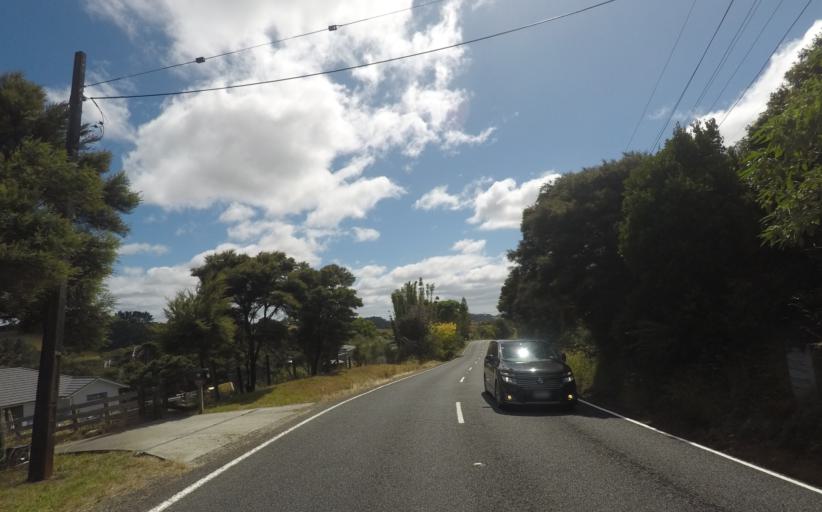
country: NZ
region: Auckland
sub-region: Auckland
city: Muriwai Beach
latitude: -36.8532
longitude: 174.5293
